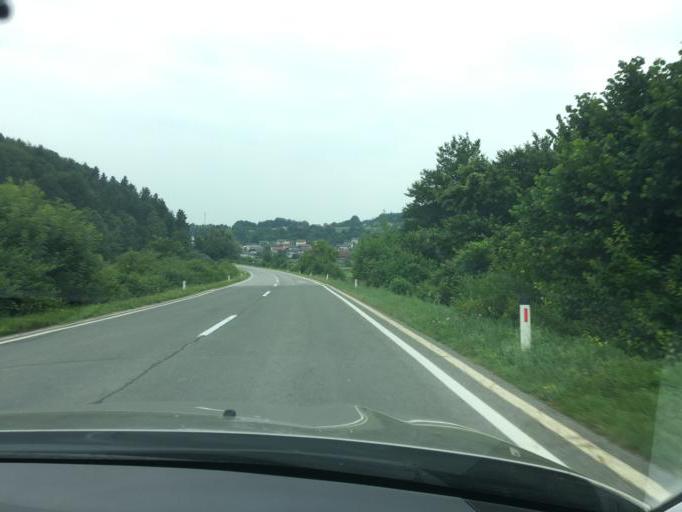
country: SI
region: Skofljica
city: Skofljica
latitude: 45.9826
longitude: 14.5899
